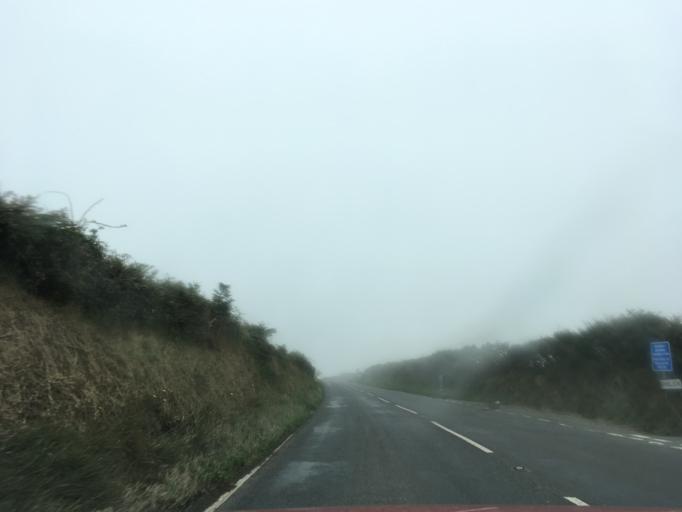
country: GB
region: Wales
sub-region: Pembrokeshire
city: Saint David's
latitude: 51.8806
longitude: -5.2272
